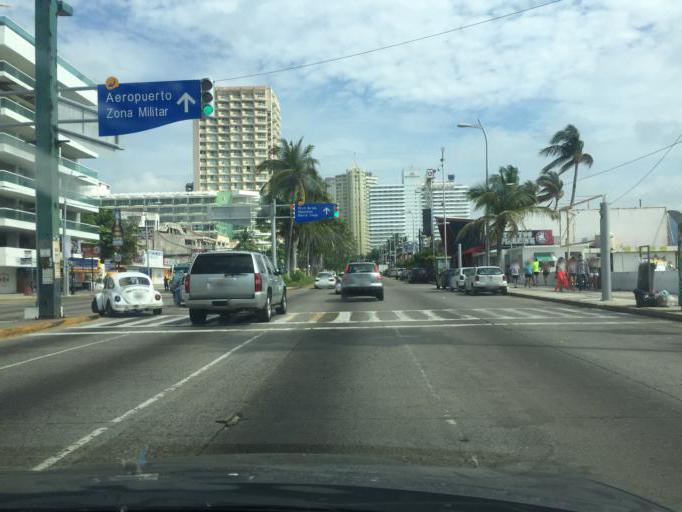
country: MX
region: Guerrero
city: Acapulco de Juarez
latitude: 16.8580
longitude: -99.8701
